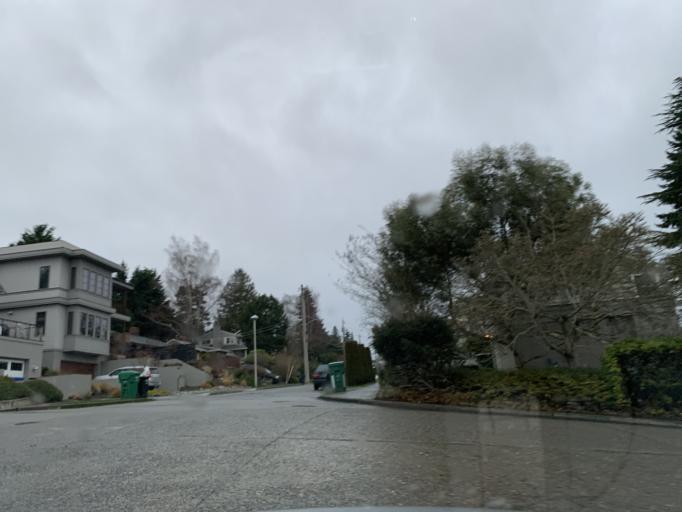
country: US
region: Washington
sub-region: King County
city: Yarrow Point
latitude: 47.6720
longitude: -122.2715
